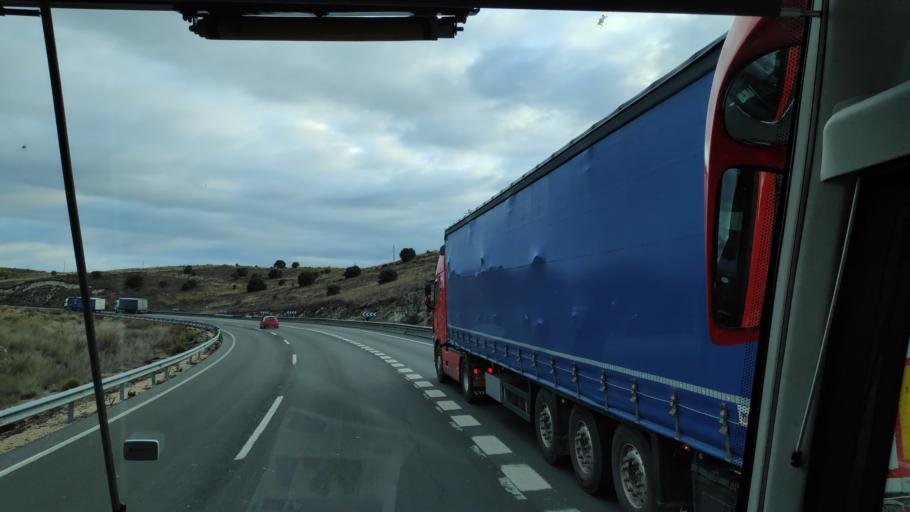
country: ES
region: Madrid
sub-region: Provincia de Madrid
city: Tielmes
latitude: 40.2011
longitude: -3.3149
